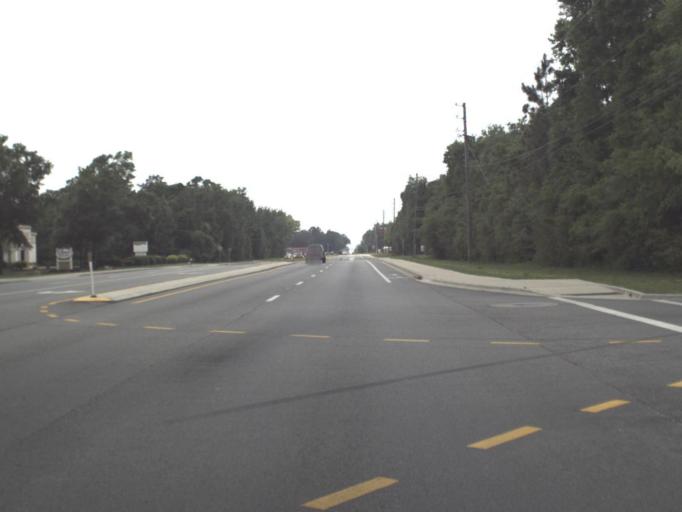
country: US
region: Florida
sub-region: Santa Rosa County
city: Bagdad
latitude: 30.5917
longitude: -87.0824
